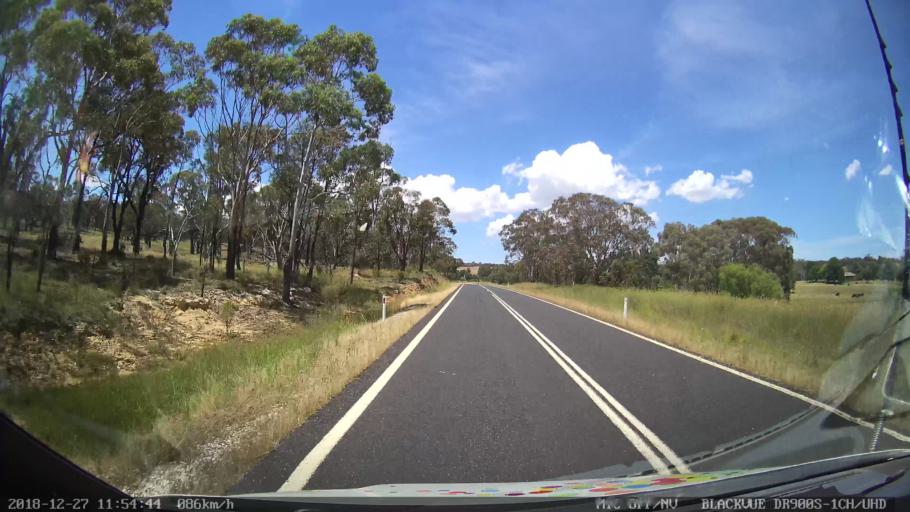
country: AU
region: New South Wales
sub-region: Blayney
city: Blayney
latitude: -33.6787
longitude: 149.4017
